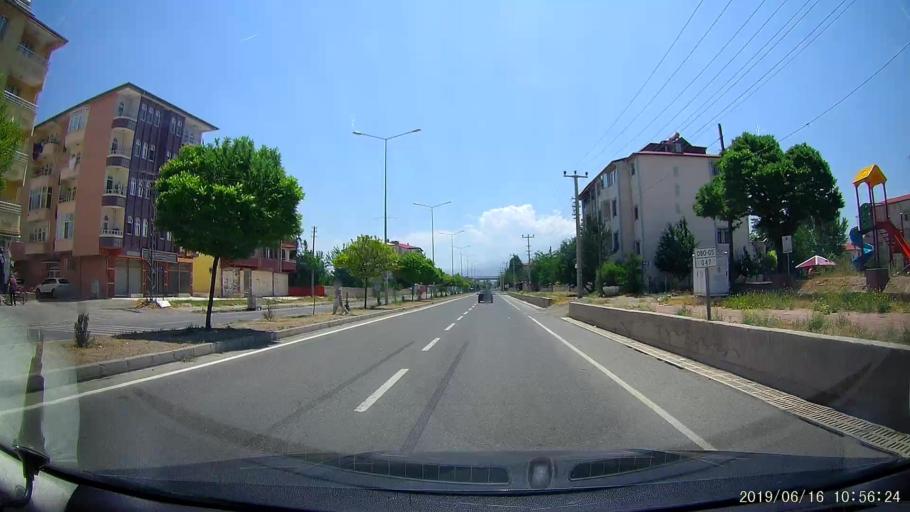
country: TR
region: Igdir
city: Igdir
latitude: 39.9301
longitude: 44.0218
